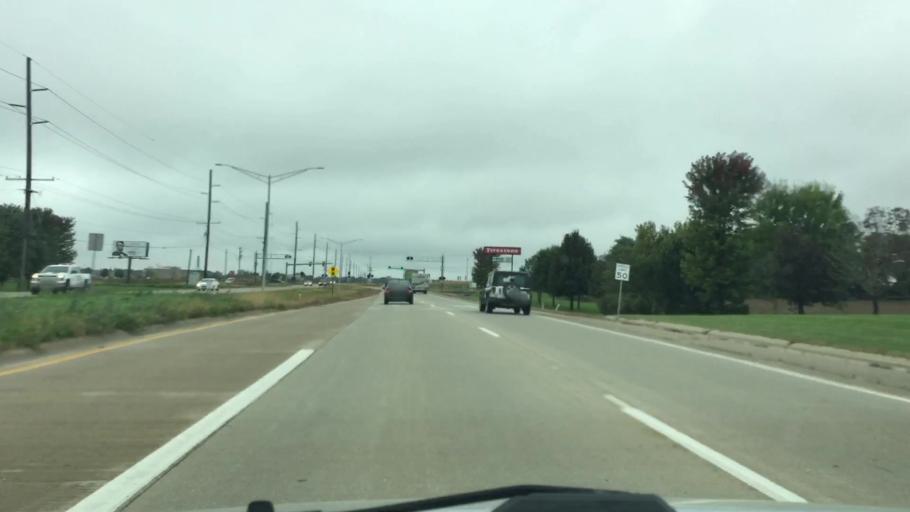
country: US
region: Wisconsin
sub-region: Rock County
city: Janesville
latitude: 42.7240
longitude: -89.0101
